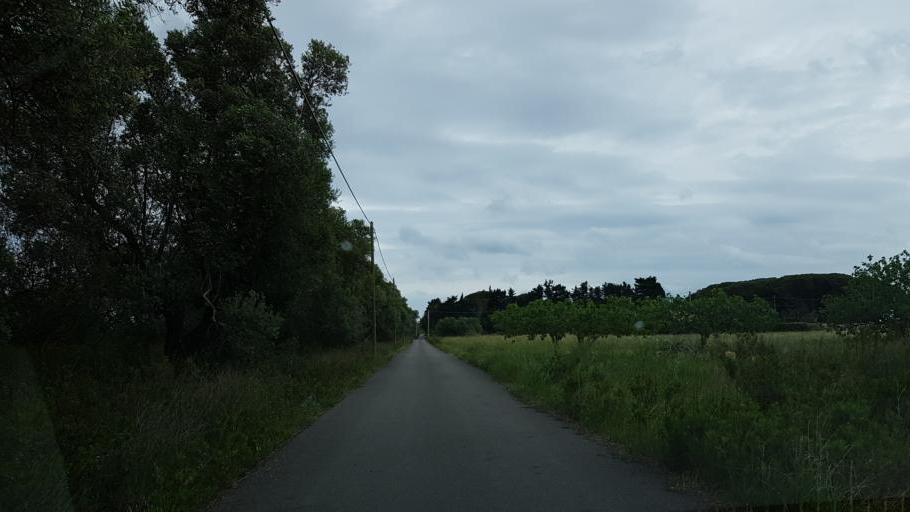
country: IT
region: Apulia
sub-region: Provincia di Brindisi
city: Brindisi
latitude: 40.6567
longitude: 17.9134
